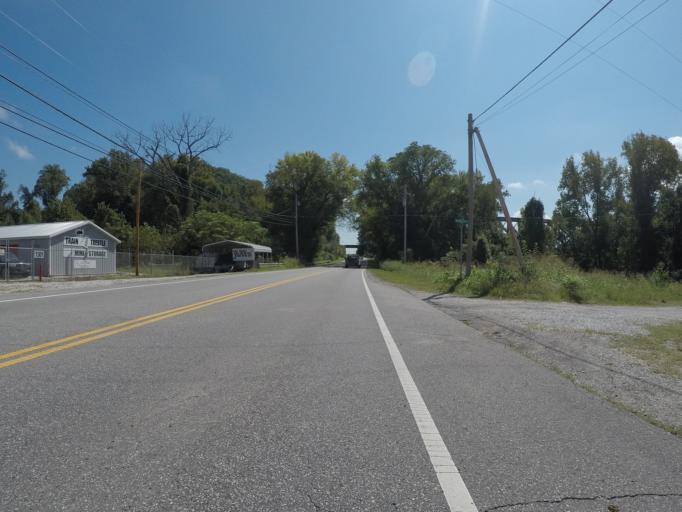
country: US
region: West Virginia
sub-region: Wayne County
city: Kenova
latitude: 38.4094
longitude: -82.5739
